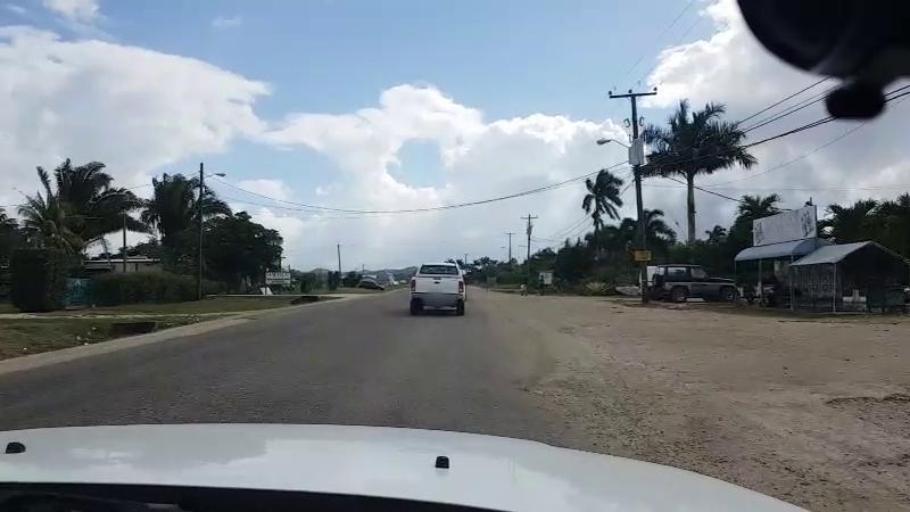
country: BZ
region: Cayo
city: Belmopan
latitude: 17.2442
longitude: -88.7832
